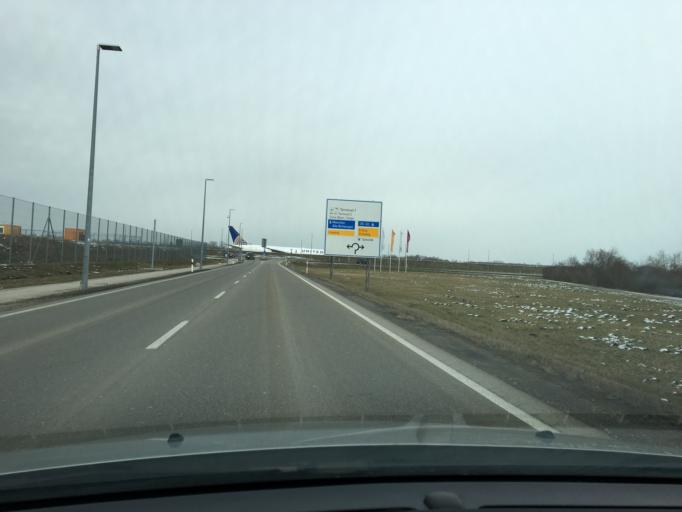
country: DE
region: Bavaria
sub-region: Upper Bavaria
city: Marzling
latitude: 48.3590
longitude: 11.8061
